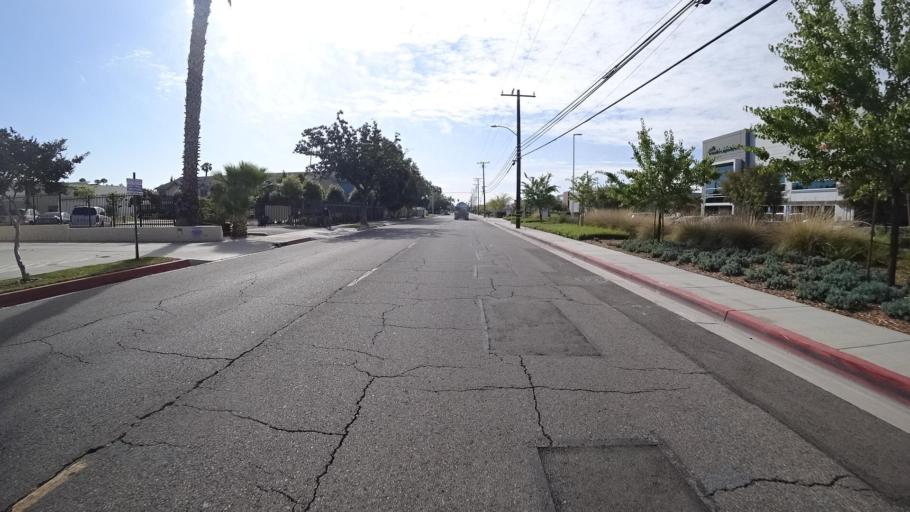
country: US
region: California
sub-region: Los Angeles County
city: West Puente Valley
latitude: 34.0357
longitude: -117.9705
